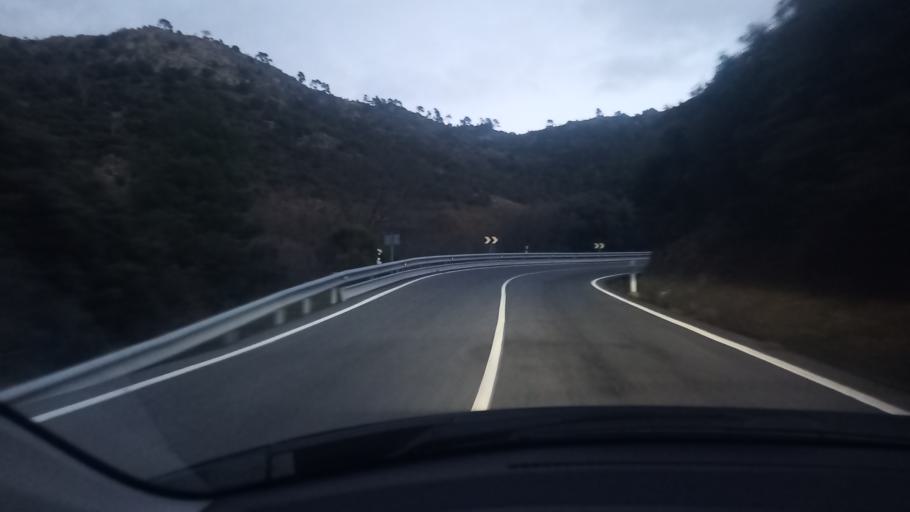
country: ES
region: Madrid
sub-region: Provincia de Madrid
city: Robledo de Chavela
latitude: 40.4626
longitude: -4.2608
